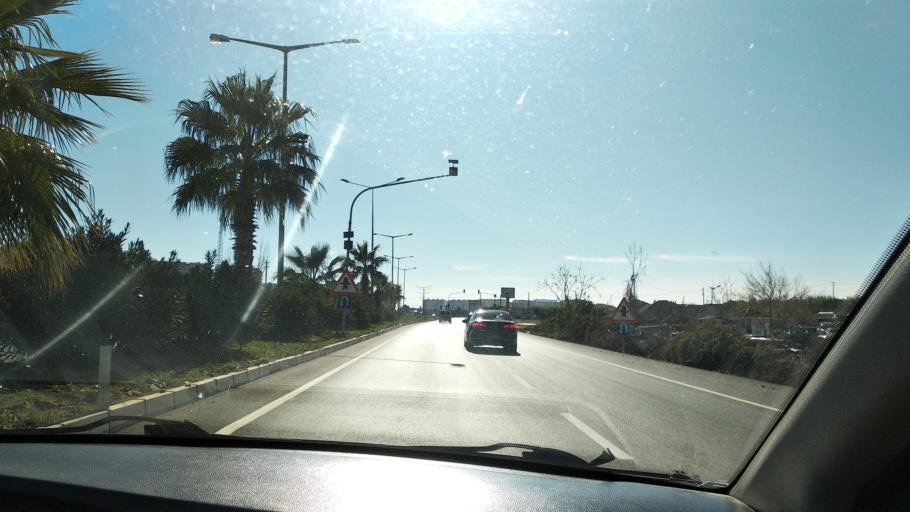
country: TR
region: Mersin
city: Tomuk
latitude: 36.6631
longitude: 34.3969
